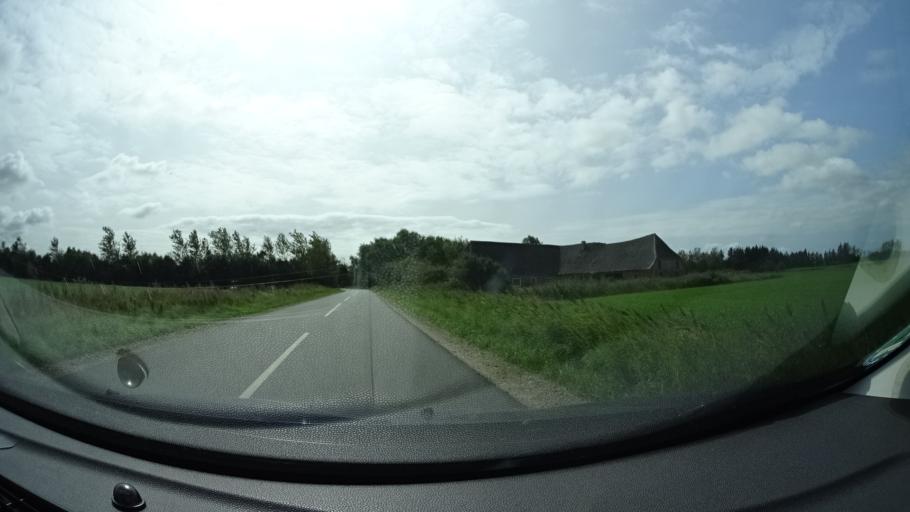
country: DK
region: South Denmark
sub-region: Tonder Kommune
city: Sherrebek
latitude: 55.0525
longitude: 8.6964
